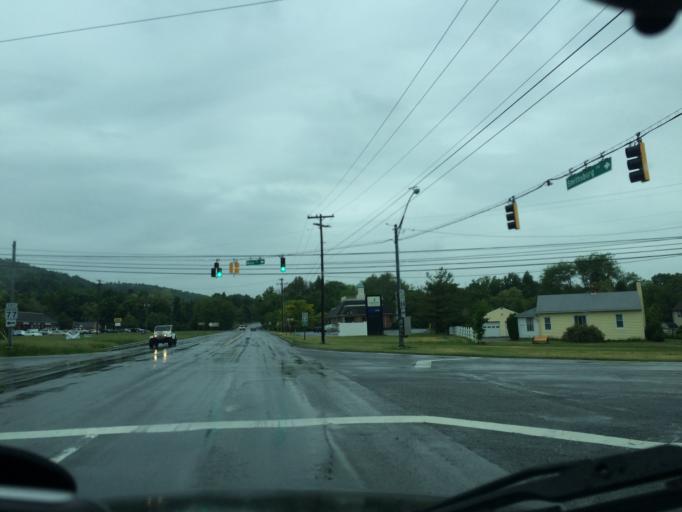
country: US
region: Maryland
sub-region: Washington County
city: Smithsburg
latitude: 39.6493
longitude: -77.5682
